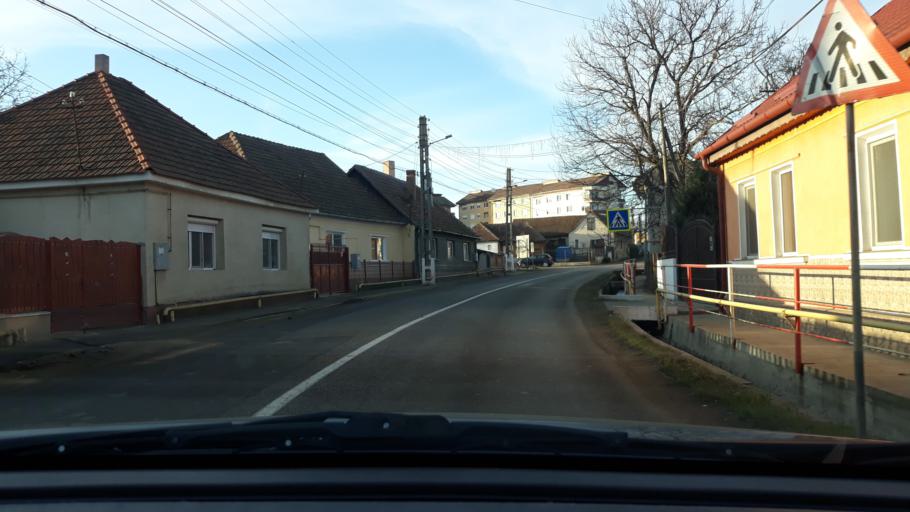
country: RO
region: Bihor
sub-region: Comuna Suplacu de Barcau
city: Suplacu de Barcau
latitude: 47.2576
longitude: 22.5279
